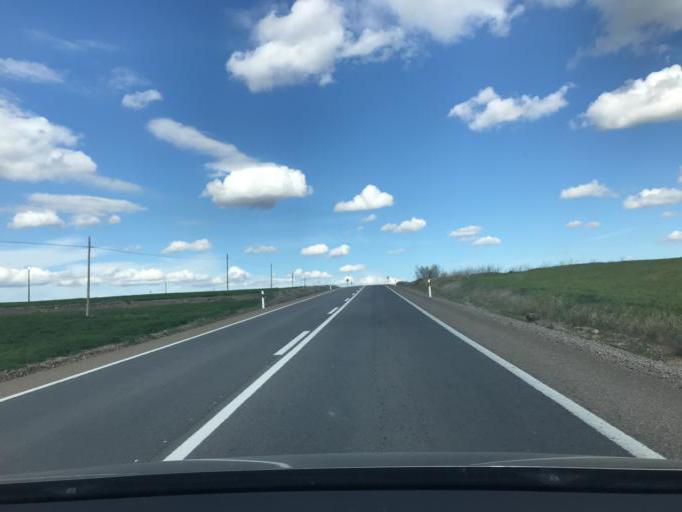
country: ES
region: Extremadura
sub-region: Provincia de Badajoz
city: Azuaga
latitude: 38.2873
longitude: -5.6575
